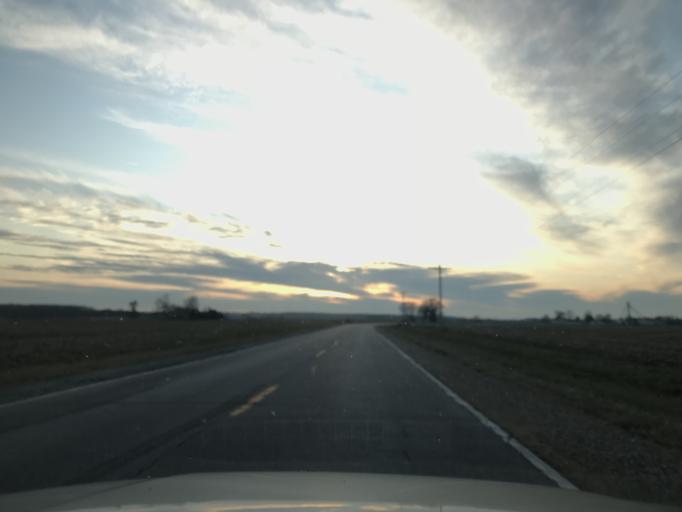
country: US
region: Illinois
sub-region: Warren County
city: Monmouth
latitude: 41.0200
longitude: -90.7896
